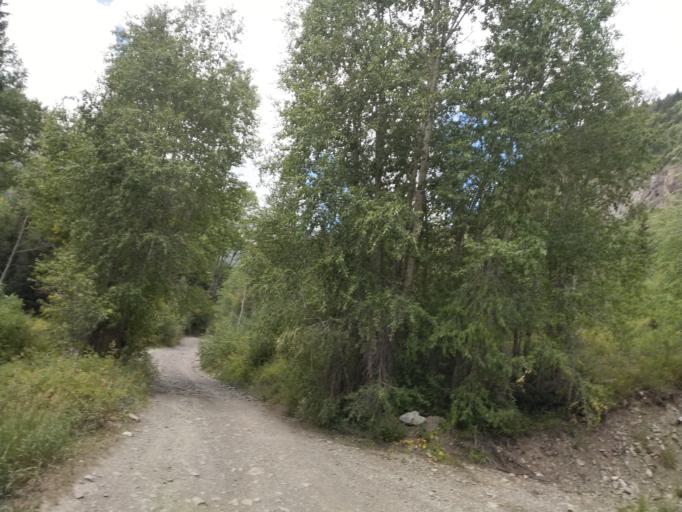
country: US
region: Colorado
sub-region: Gunnison County
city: Crested Butte
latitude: 39.0567
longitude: -107.1136
